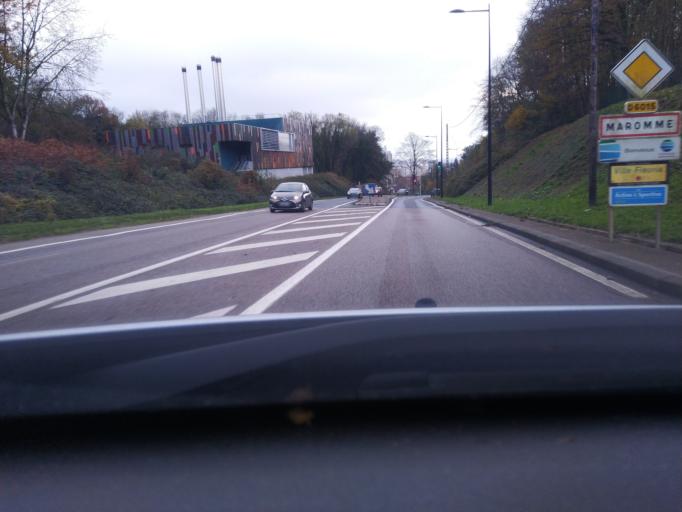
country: FR
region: Haute-Normandie
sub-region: Departement de la Seine-Maritime
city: Maromme
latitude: 49.4853
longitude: 1.0342
